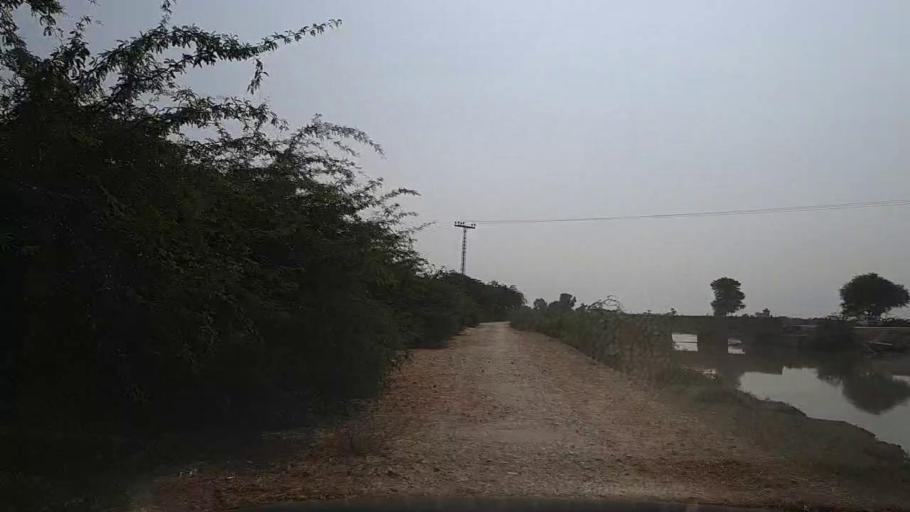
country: PK
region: Sindh
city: Chuhar Jamali
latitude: 24.5412
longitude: 67.9125
